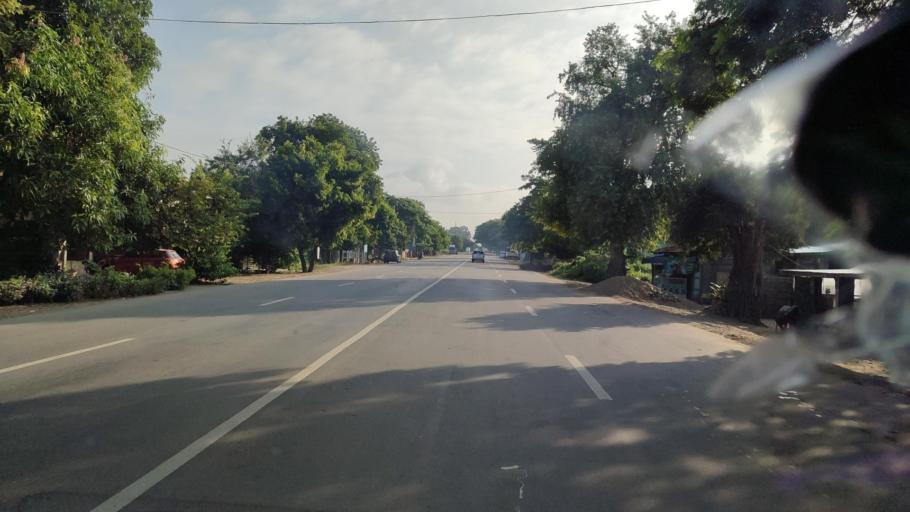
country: MM
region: Mandalay
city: Yamethin
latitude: 20.7526
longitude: 96.2408
